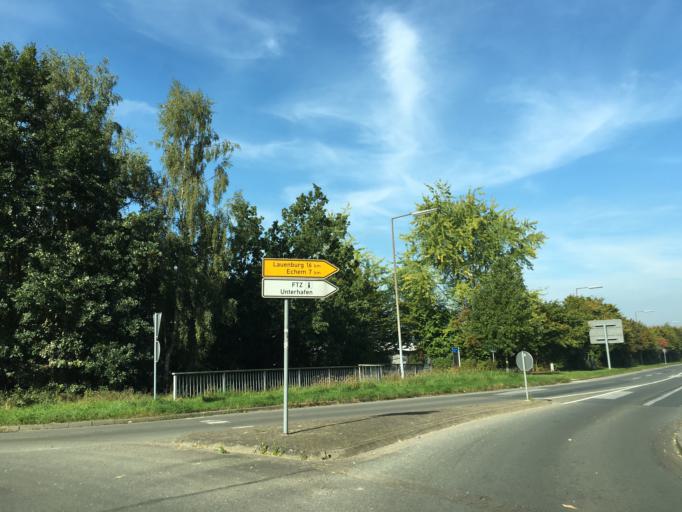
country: DE
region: Lower Saxony
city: Scharnebeck
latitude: 53.2916
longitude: 10.4905
